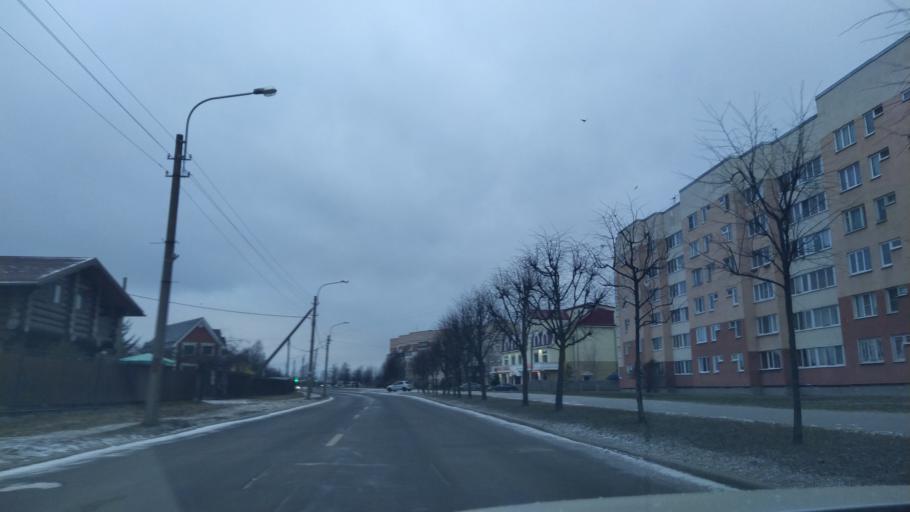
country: RU
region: St.-Petersburg
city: Pushkin
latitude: 59.7326
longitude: 30.3998
